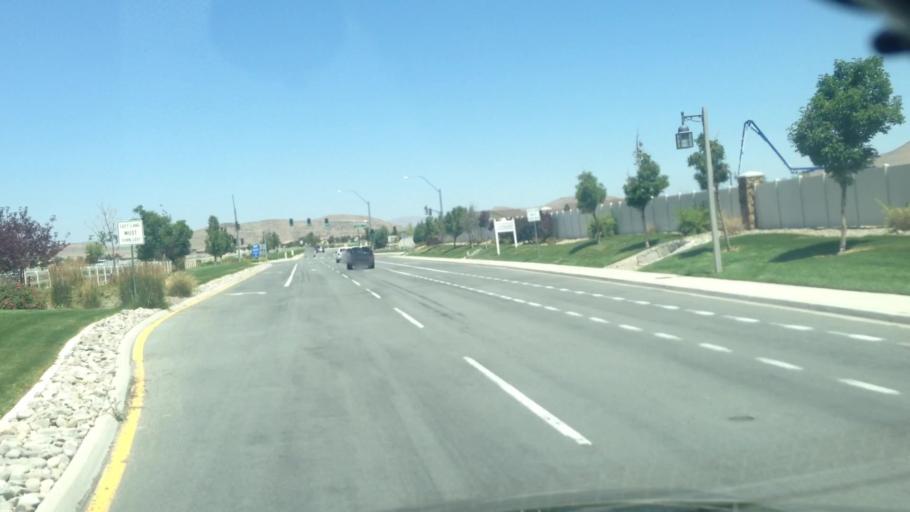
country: US
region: Nevada
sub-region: Washoe County
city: Sparks
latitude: 39.4346
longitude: -119.7292
